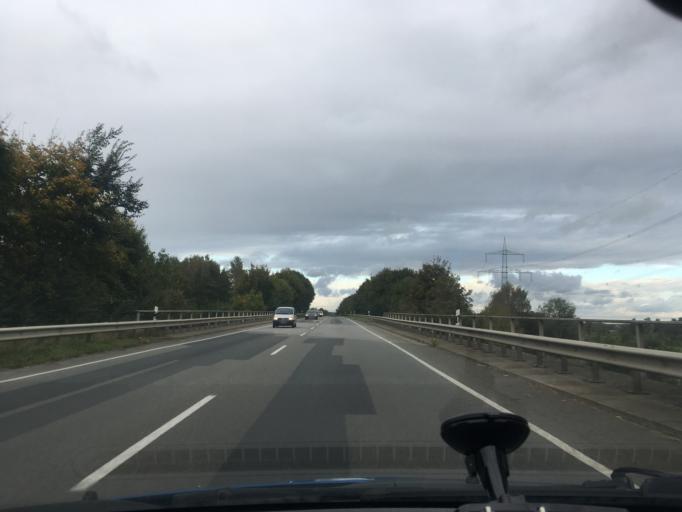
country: DE
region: Lower Saxony
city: Handorf
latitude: 53.3538
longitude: 10.3406
